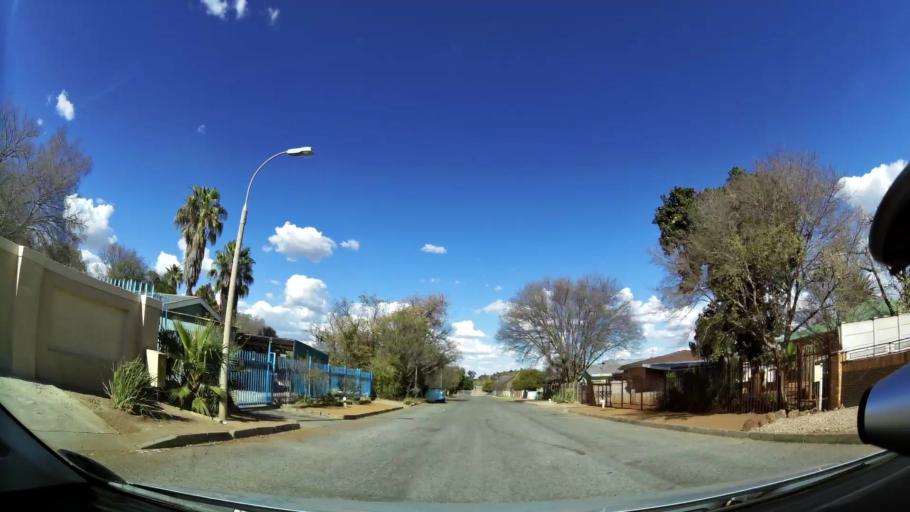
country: ZA
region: North-West
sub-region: Dr Kenneth Kaunda District Municipality
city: Klerksdorp
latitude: -26.8613
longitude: 26.6465
